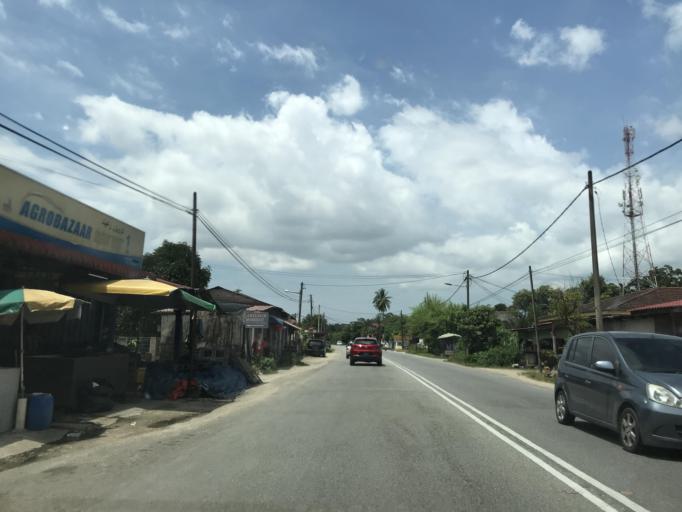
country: MY
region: Kelantan
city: Pasir Mas
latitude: 6.0561
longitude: 102.1962
